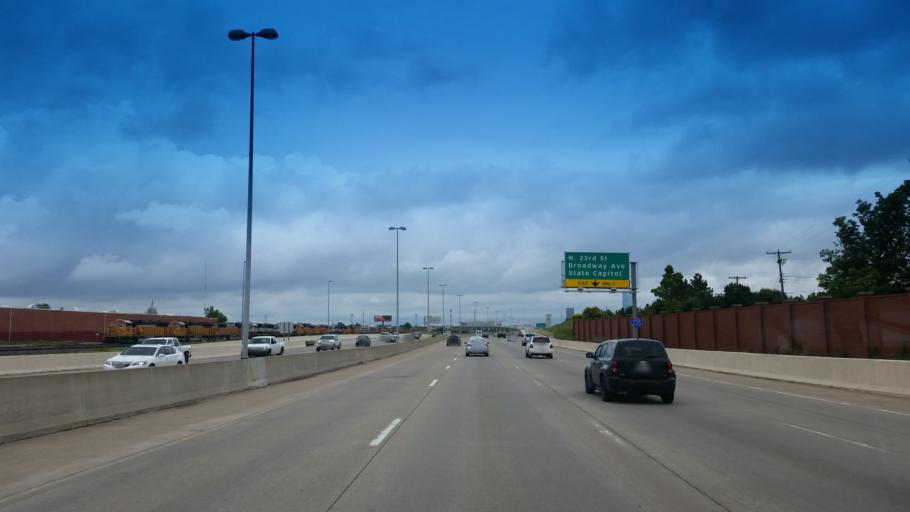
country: US
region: Oklahoma
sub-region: Oklahoma County
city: Oklahoma City
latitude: 35.5074
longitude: -97.5146
